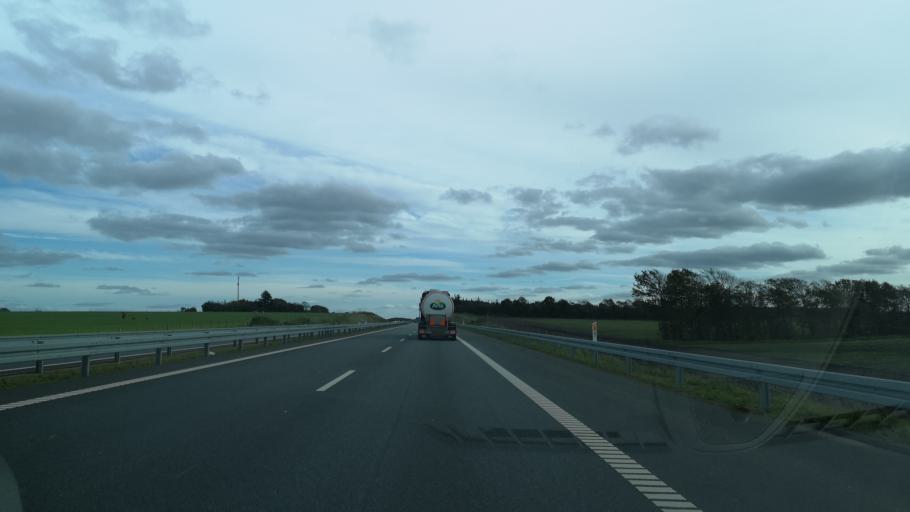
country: DK
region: Central Jutland
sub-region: Herning Kommune
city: Avlum
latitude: 56.2732
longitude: 8.7484
